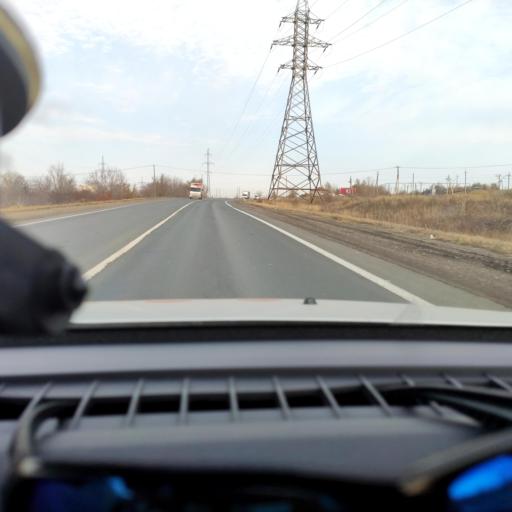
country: RU
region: Samara
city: Chapayevsk
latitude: 52.9914
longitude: 49.7671
